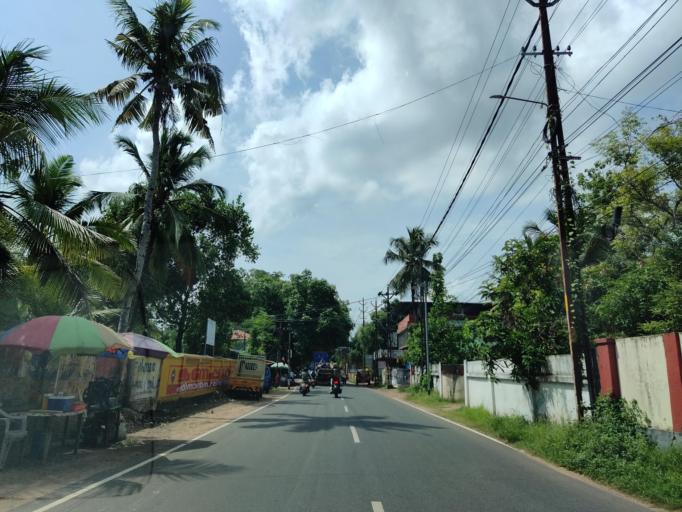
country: IN
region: Kerala
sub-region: Alappuzha
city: Mavelikara
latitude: 9.2576
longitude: 76.5450
